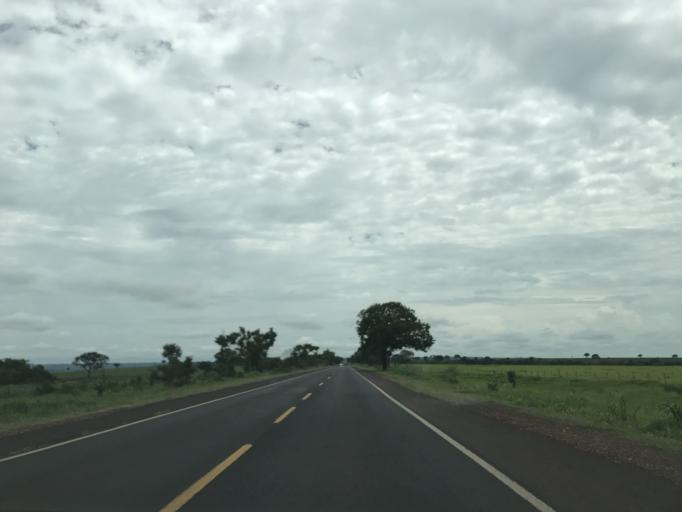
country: BR
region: Minas Gerais
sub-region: Frutal
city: Frutal
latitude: -19.9695
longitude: -48.9985
